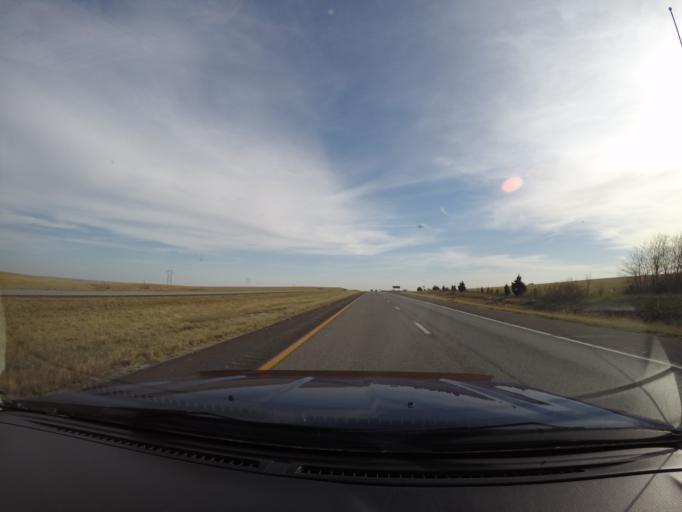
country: US
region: Kansas
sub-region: Riley County
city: Manhattan
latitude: 39.1381
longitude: -96.5383
